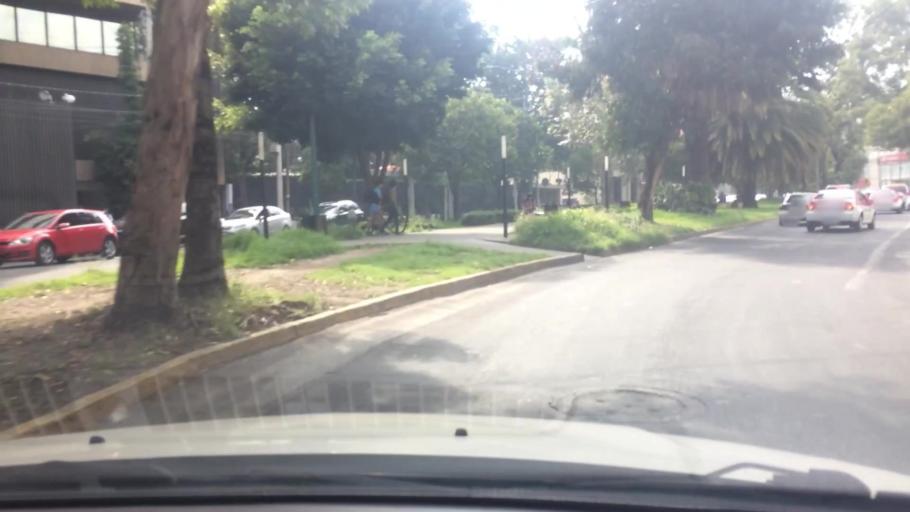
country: MX
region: Mexico City
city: Alvaro Obregon
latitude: 19.3618
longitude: -99.1838
